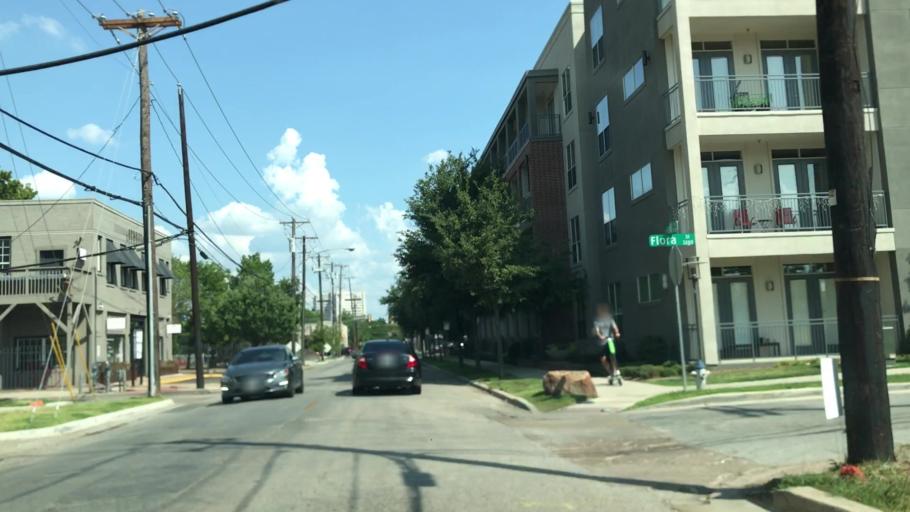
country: US
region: Texas
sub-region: Dallas County
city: Dallas
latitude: 32.7964
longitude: -96.7903
